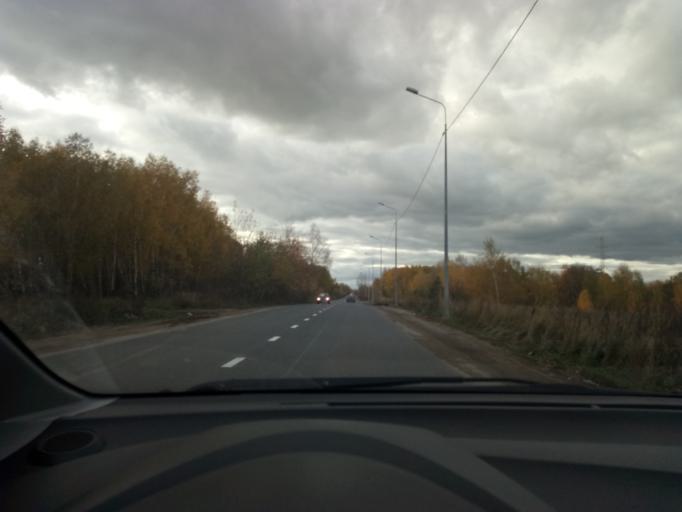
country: RU
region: Tatarstan
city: Staroye Arakchino
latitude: 55.8848
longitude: 48.9923
